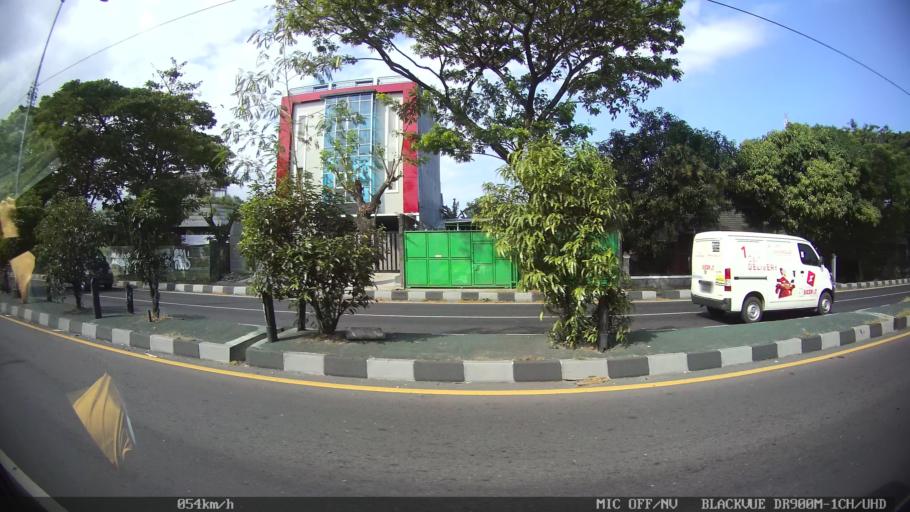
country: ID
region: Daerah Istimewa Yogyakarta
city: Sewon
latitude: -7.8358
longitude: 110.3891
